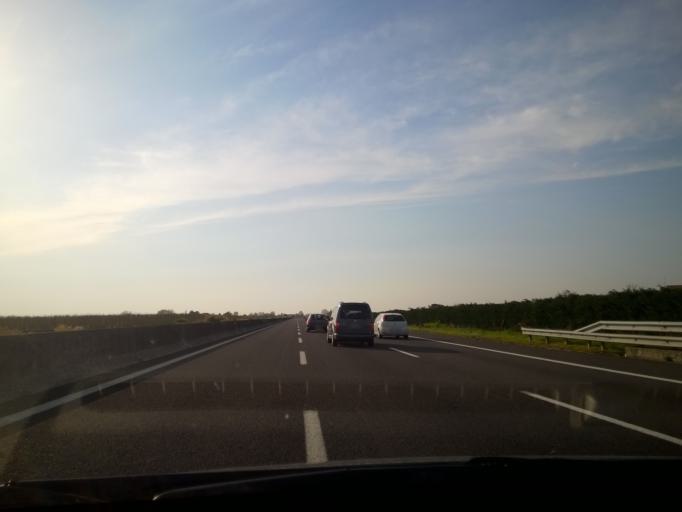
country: IT
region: Emilia-Romagna
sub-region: Provincia di Ravenna
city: Granarolo
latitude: 44.3035
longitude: 11.9541
